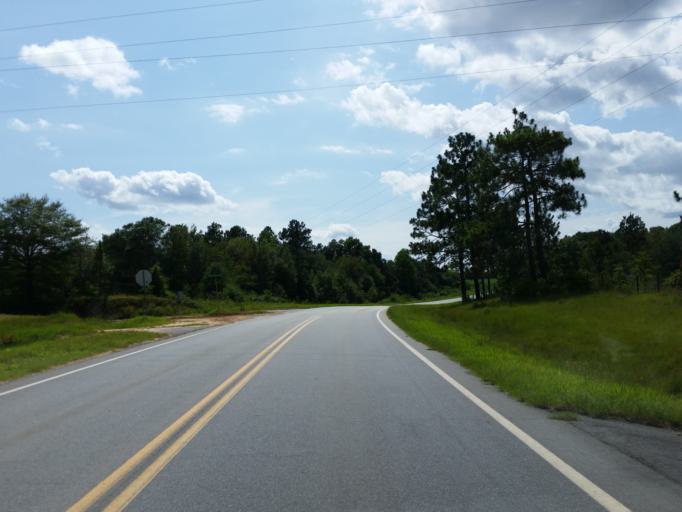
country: US
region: Georgia
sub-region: Turner County
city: Ashburn
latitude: 31.6349
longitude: -83.5118
